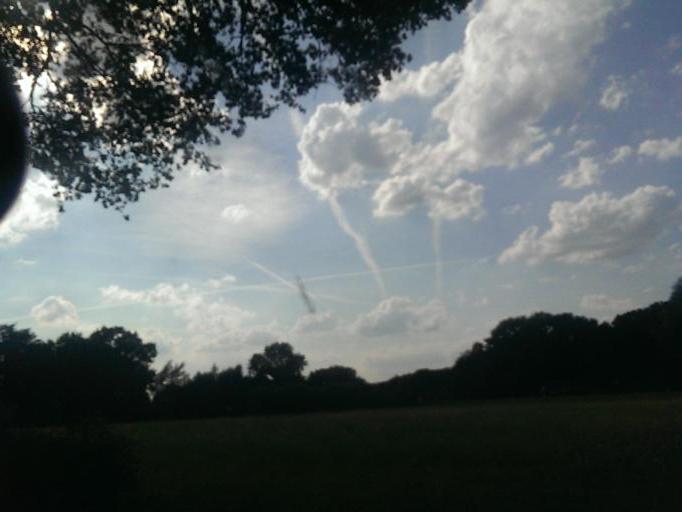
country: DE
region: North Rhine-Westphalia
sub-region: Regierungsbezirk Detmold
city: Hovelhof
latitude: 51.7608
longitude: 8.6358
